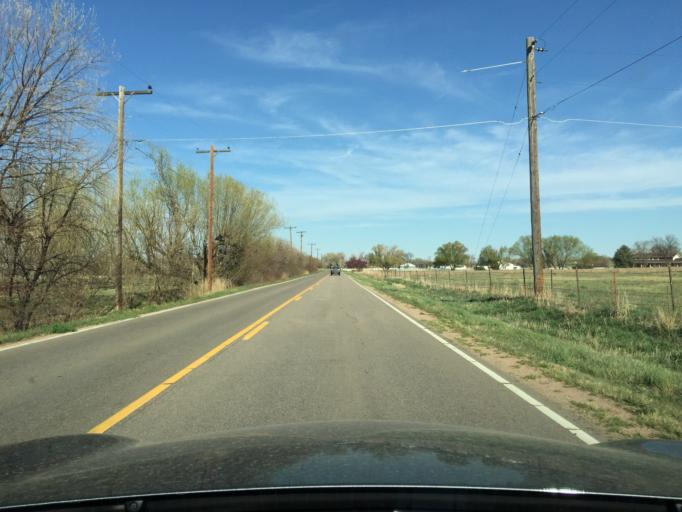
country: US
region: Colorado
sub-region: Boulder County
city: Erie
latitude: 40.0546
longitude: -105.0976
